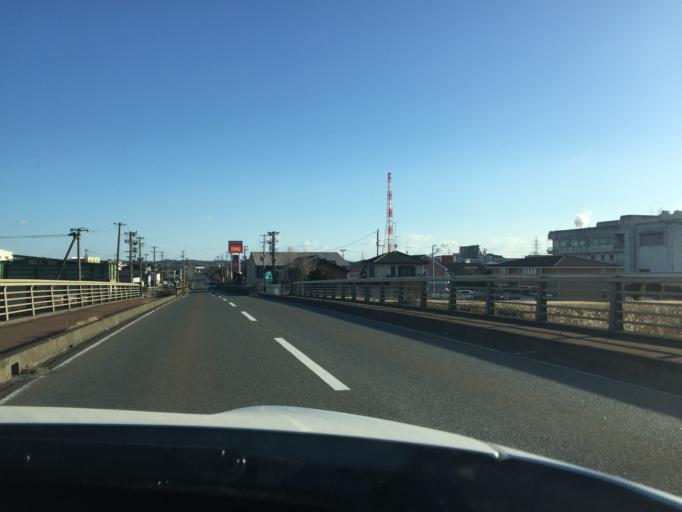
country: JP
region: Fukushima
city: Iwaki
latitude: 36.9403
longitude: 140.8706
